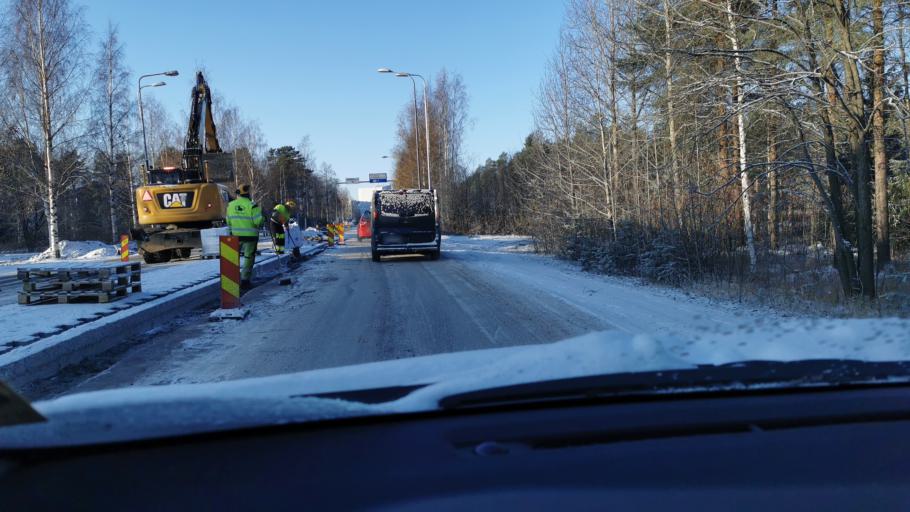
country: FI
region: Northern Ostrobothnia
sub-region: Oulu
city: Oulu
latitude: 65.0557
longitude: 25.4719
